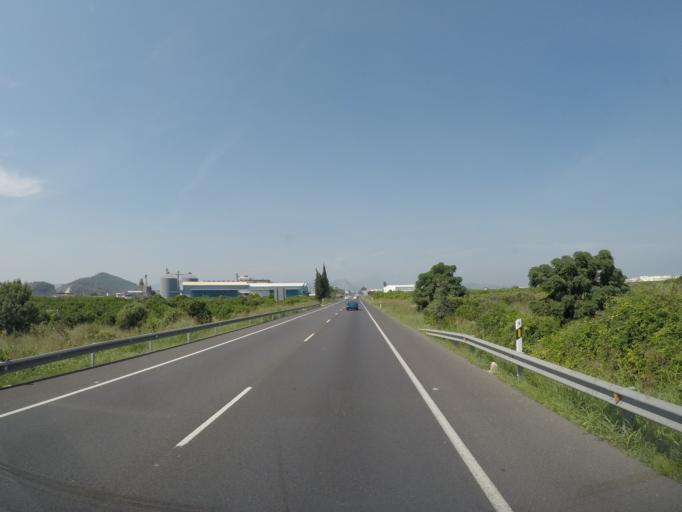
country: ES
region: Valencia
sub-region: Provincia de Valencia
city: Oliva
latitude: 38.9266
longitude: -0.1292
